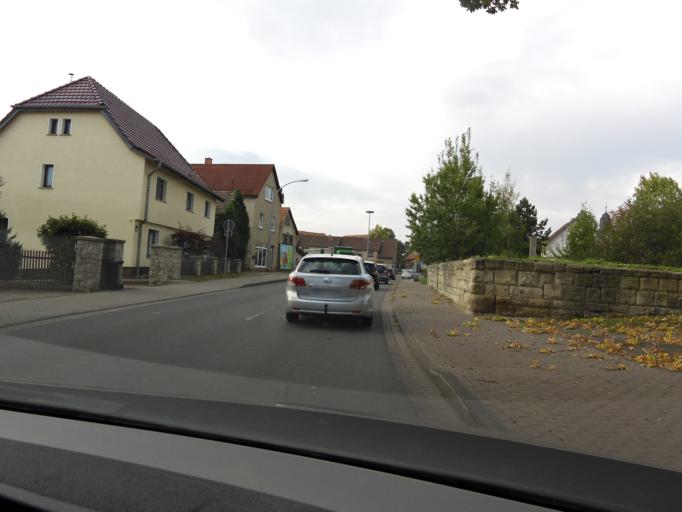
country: DE
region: Thuringia
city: Barchfeld
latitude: 50.7986
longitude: 10.2988
